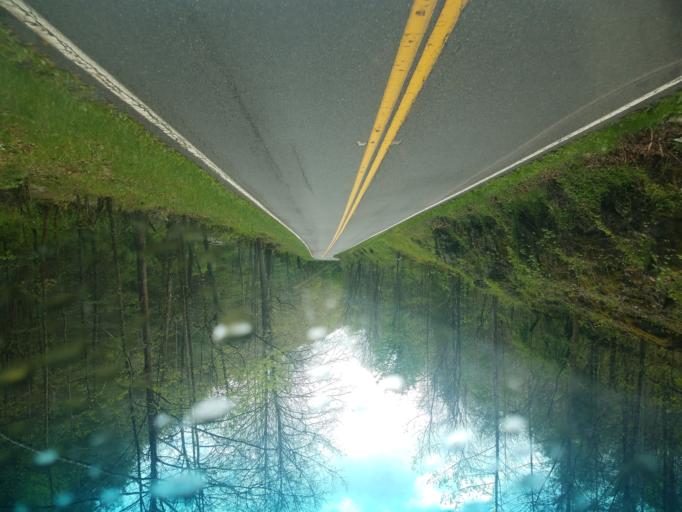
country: US
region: Virginia
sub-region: Smyth County
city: Marion
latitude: 36.9431
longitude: -81.5300
